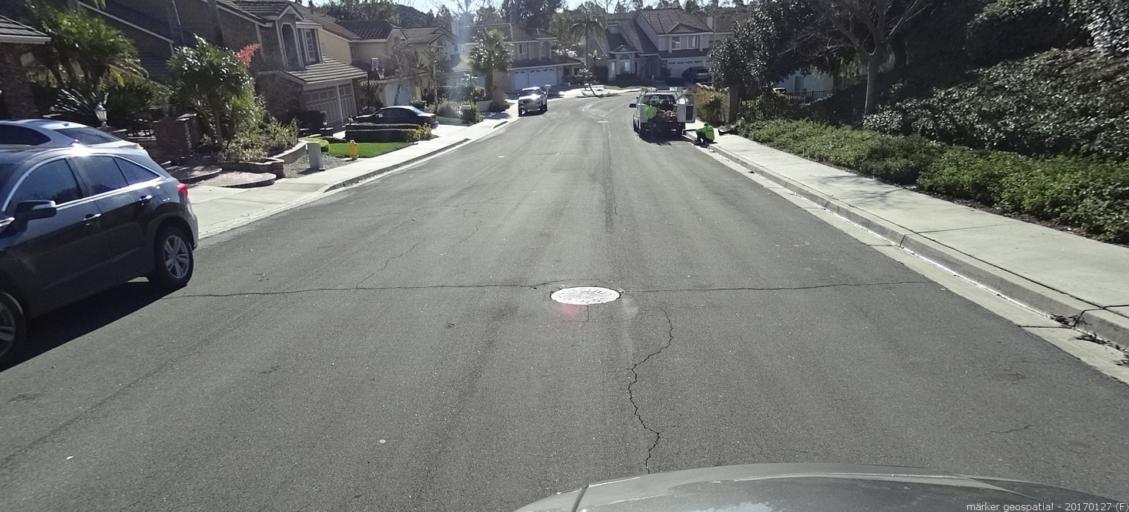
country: US
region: California
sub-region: Orange County
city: Foothill Ranch
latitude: 33.6577
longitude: -117.6600
